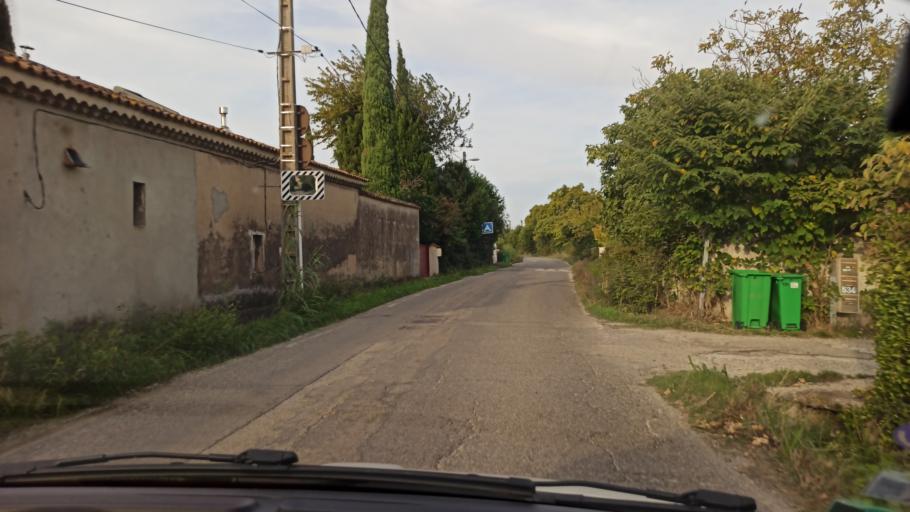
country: FR
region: Provence-Alpes-Cote d'Azur
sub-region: Departement du Vaucluse
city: Montfavet
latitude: 43.9349
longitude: 4.8659
